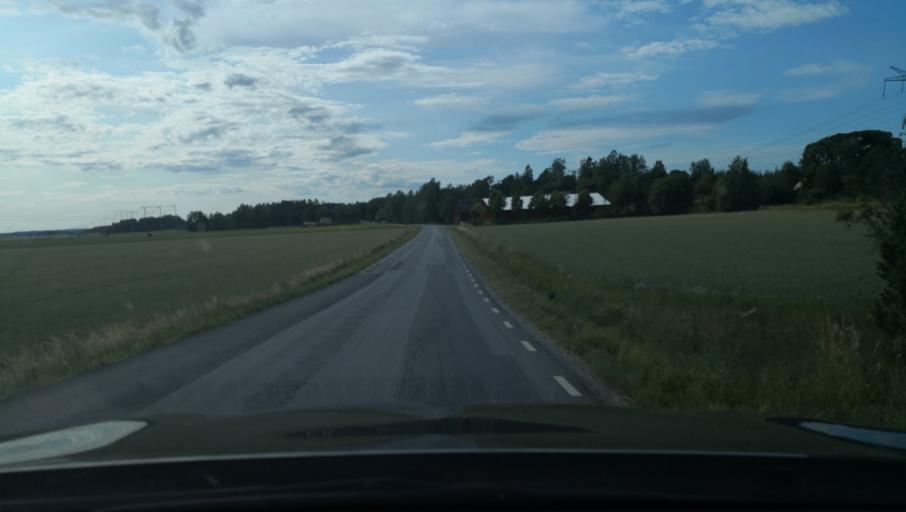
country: SE
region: Uppsala
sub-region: Enkopings Kommun
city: Orsundsbro
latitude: 59.6845
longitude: 17.3974
